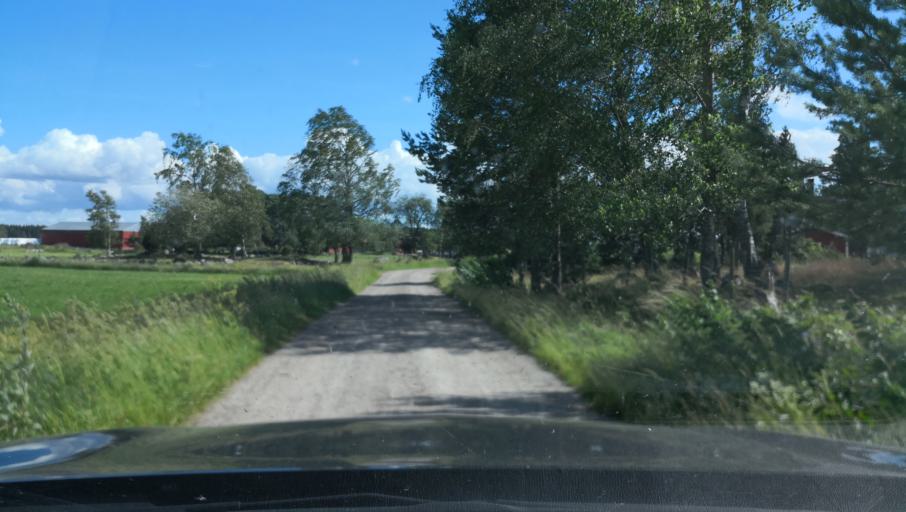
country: SE
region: Vaestmanland
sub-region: Kungsors Kommun
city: Kungsoer
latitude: 59.3237
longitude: 16.0567
